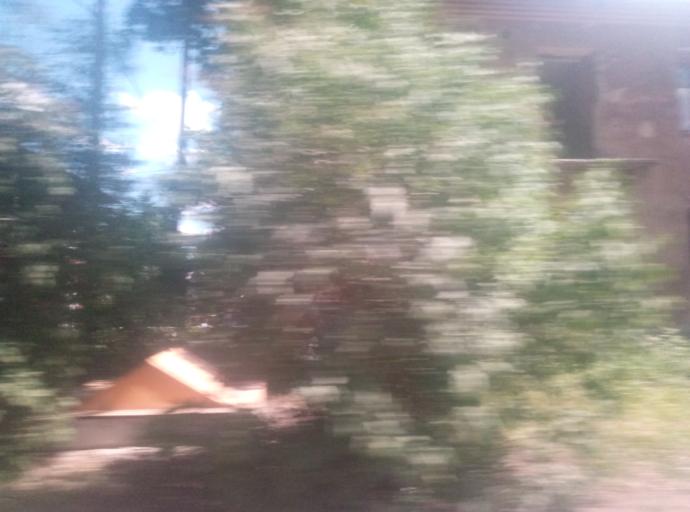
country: RU
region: Tula
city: Kireyevsk
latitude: 53.9258
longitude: 37.9225
